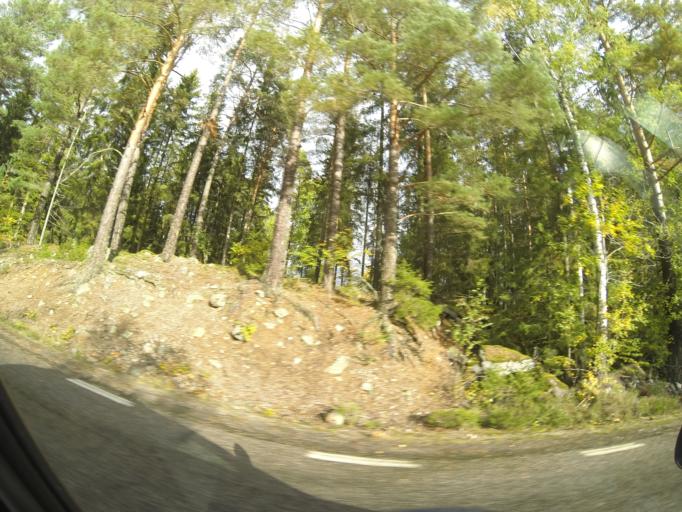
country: SE
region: Soedermanland
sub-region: Eskilstuna Kommun
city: Kvicksund
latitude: 59.3253
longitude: 16.2620
